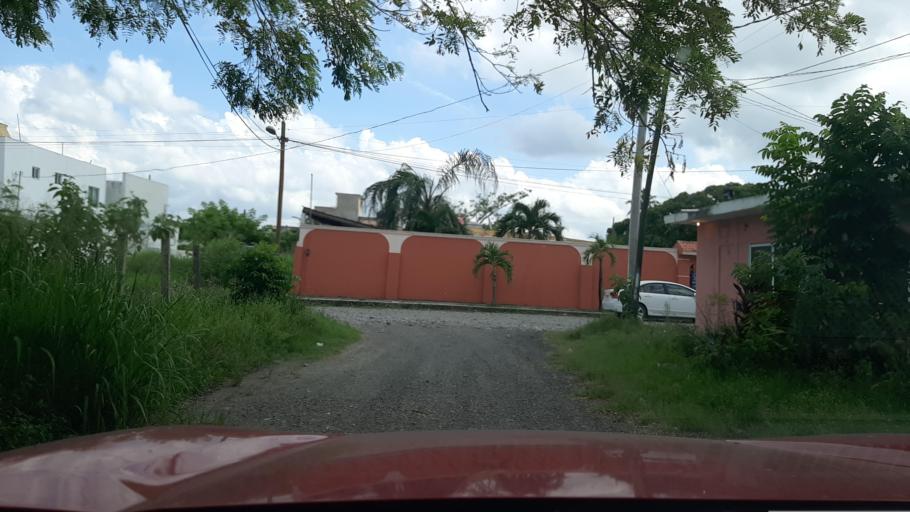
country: MX
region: Veracruz
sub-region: Poza Rica de Hidalgo
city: Villa de las Flores
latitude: 20.5739
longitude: -97.4337
